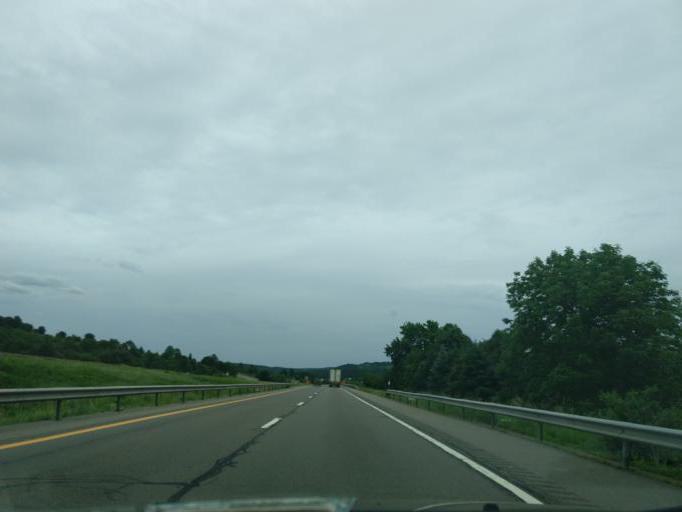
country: US
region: New York
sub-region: Chenango County
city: Lakeview
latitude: 42.4115
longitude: -76.0162
